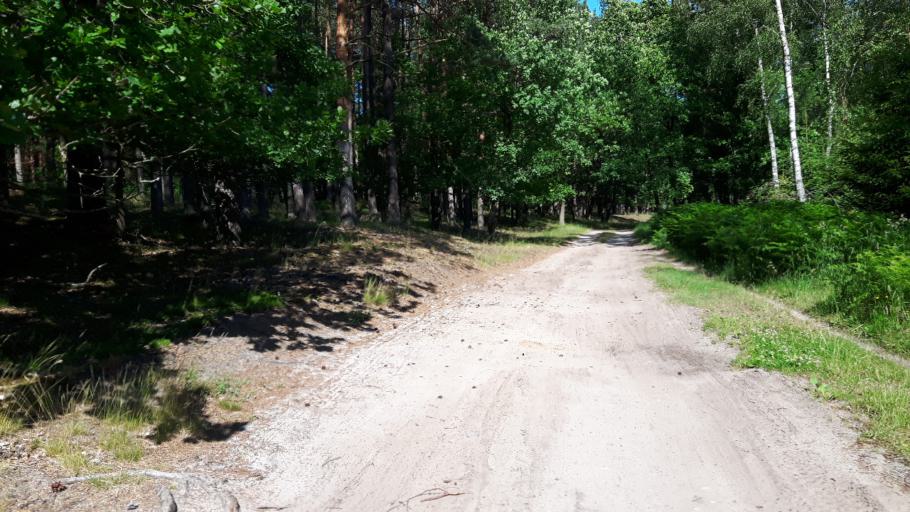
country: PL
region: Pomeranian Voivodeship
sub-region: Powiat leborski
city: Leba
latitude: 54.6991
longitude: 17.4933
